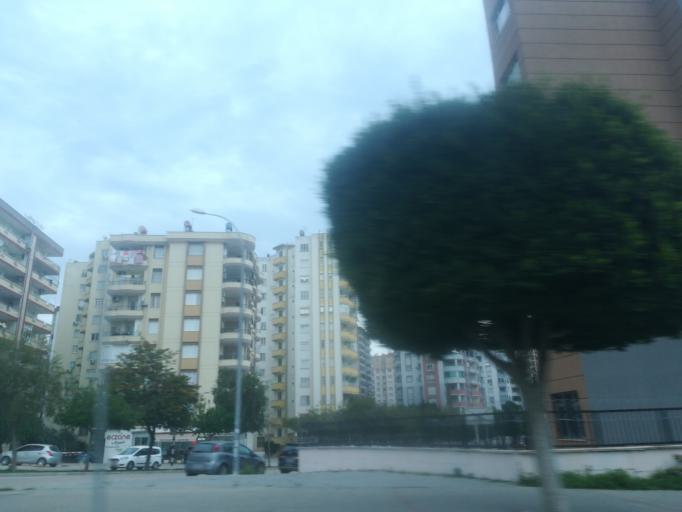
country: TR
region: Adana
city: Adana
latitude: 37.0428
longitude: 35.2916
